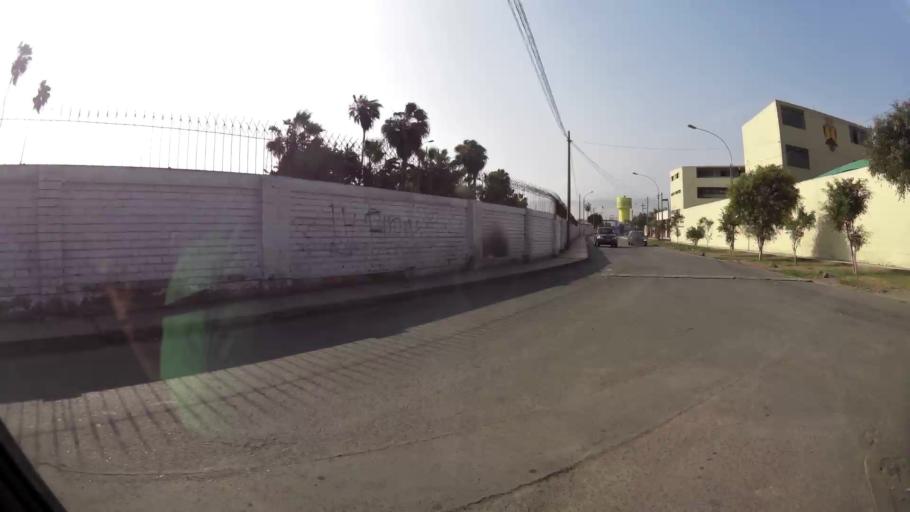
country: PE
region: Lima
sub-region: Lima
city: Santa Rosa
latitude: -11.7716
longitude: -77.1726
